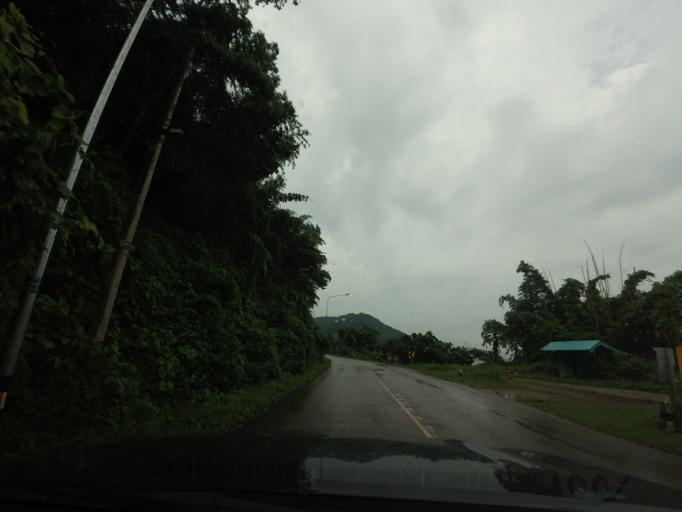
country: TH
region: Nong Khai
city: Sangkhom
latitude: 18.2089
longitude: 102.1341
